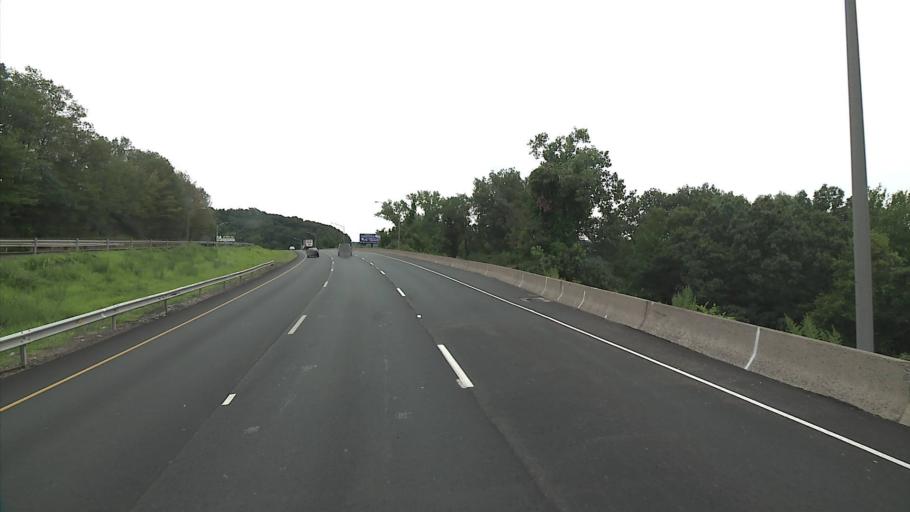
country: US
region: Connecticut
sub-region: New Haven County
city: Waterbury
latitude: 41.5257
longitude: -73.0438
